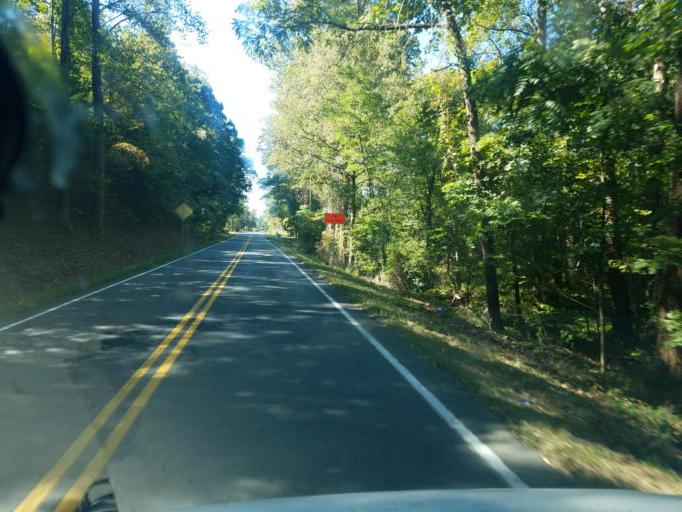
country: US
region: Virginia
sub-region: Greene County
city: Stanardsville
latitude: 38.3282
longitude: -78.4073
